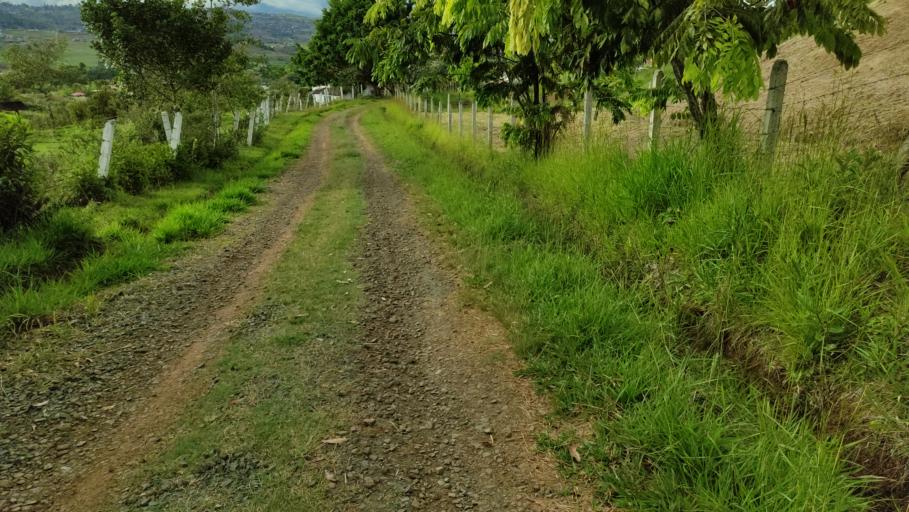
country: CO
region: Valle del Cauca
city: Dagua
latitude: 3.5386
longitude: -76.6431
